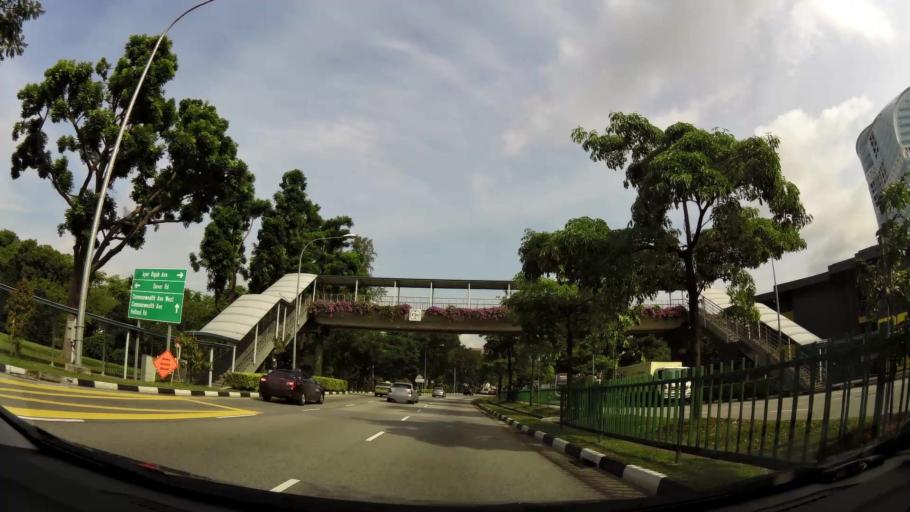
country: SG
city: Singapore
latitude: 1.2979
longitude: 103.7855
